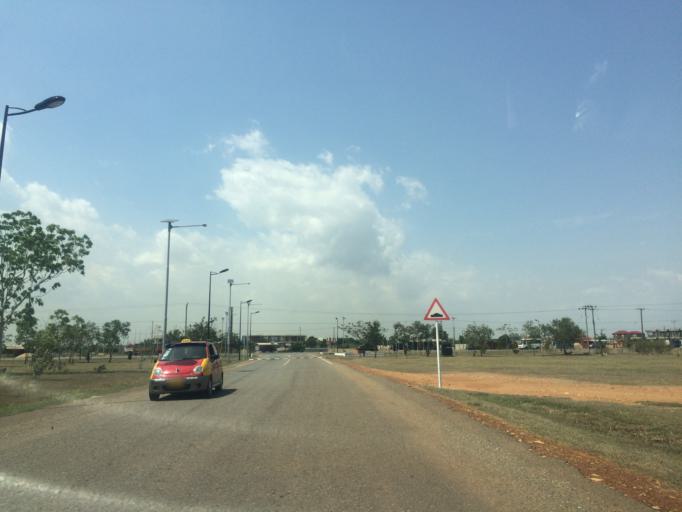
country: GH
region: Greater Accra
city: Tema
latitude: 5.7748
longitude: 0.0830
